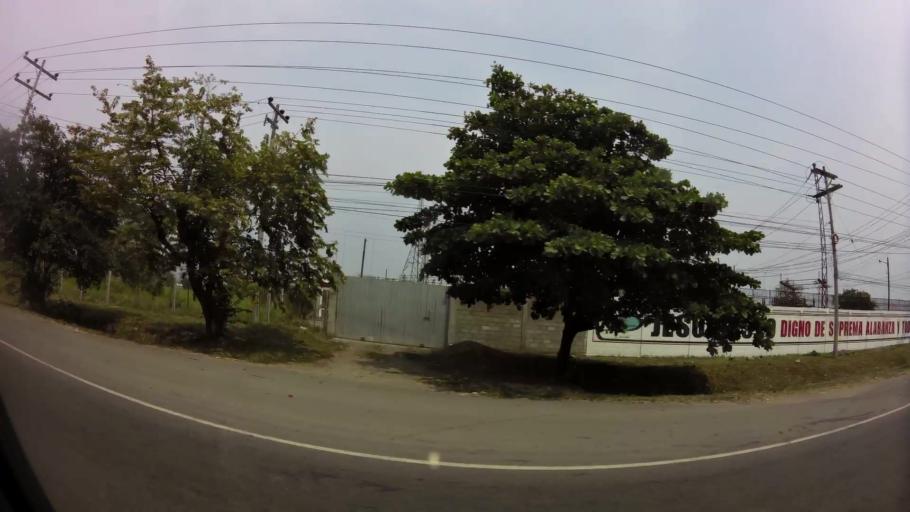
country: HN
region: Cortes
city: Villanueva
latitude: 15.3389
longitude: -87.9875
